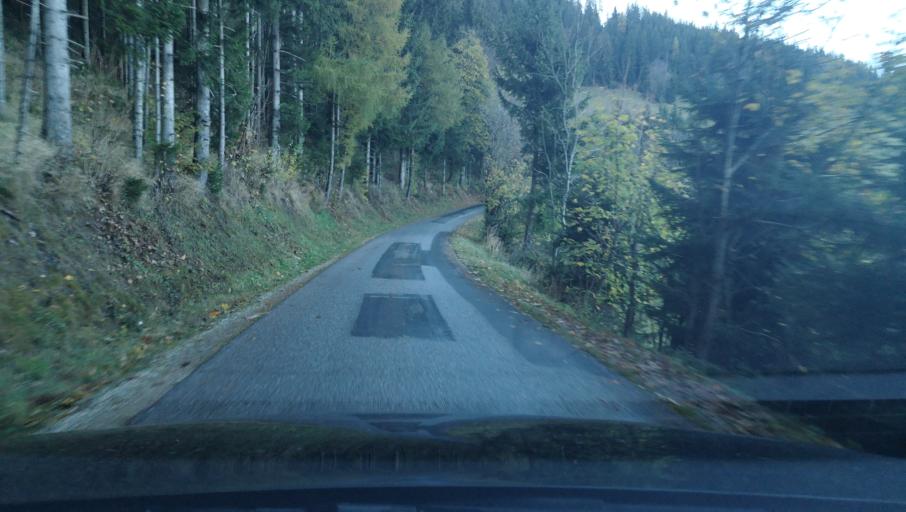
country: AT
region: Styria
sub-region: Politischer Bezirk Weiz
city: Birkfeld
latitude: 47.3344
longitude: 15.6490
